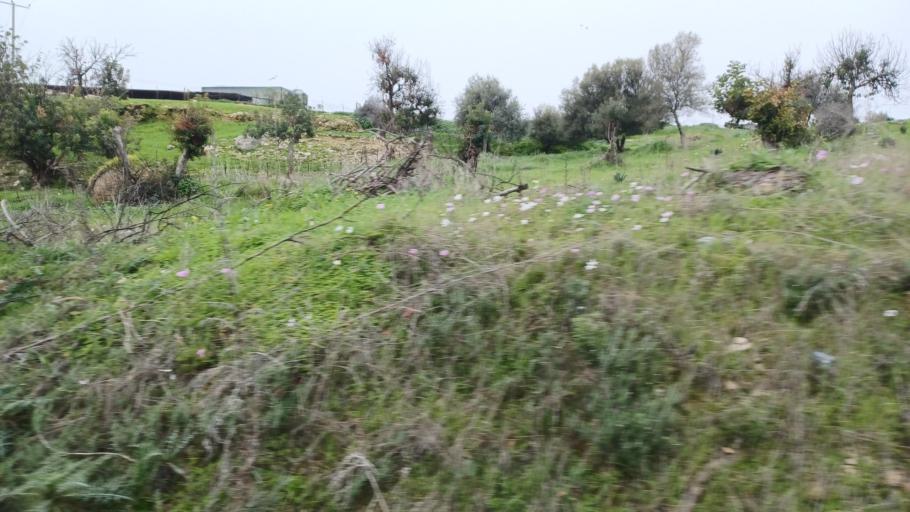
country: CY
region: Limassol
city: Pissouri
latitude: 34.6979
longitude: 32.7584
